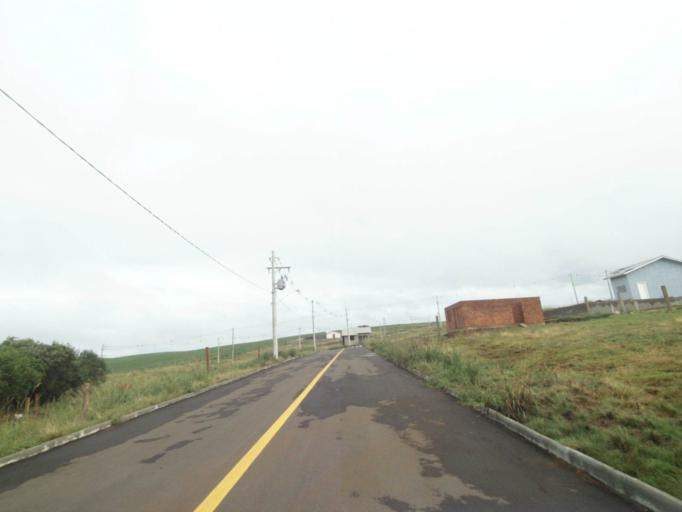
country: BR
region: Rio Grande do Sul
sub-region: Lagoa Vermelha
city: Lagoa Vermelha
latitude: -28.2291
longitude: -51.5217
